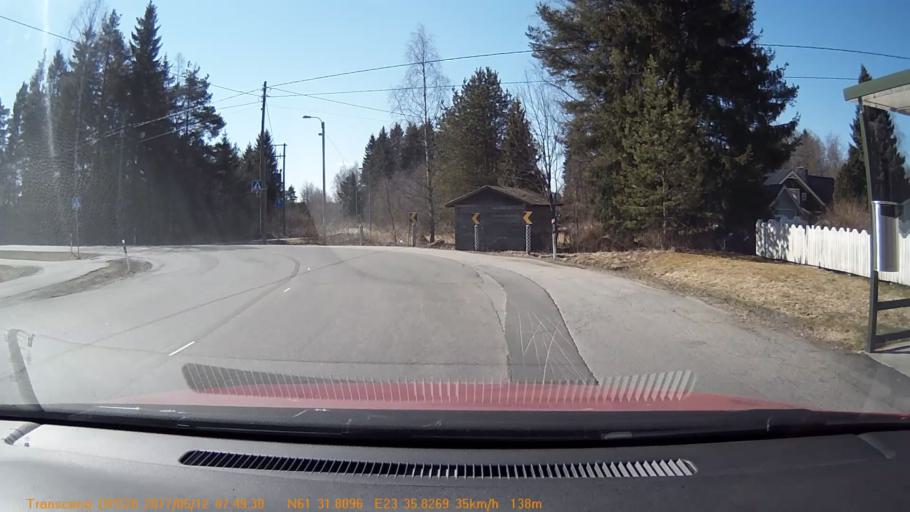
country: FI
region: Pirkanmaa
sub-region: Tampere
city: Yloejaervi
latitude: 61.5302
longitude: 23.5971
